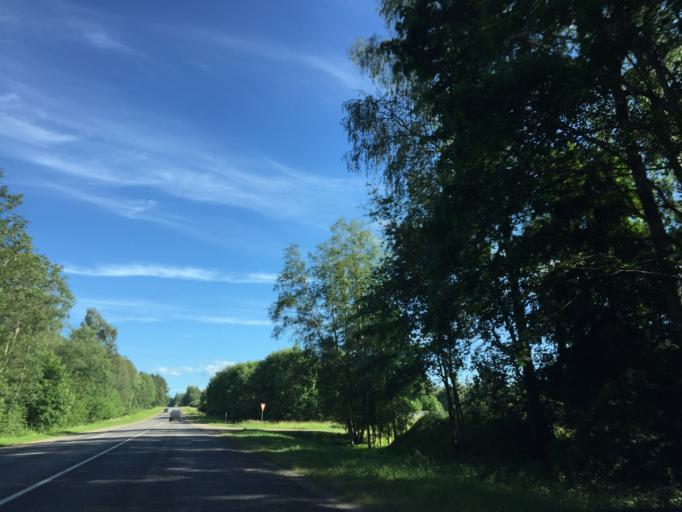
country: LV
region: Kuldigas Rajons
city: Kuldiga
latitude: 57.0593
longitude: 21.8147
